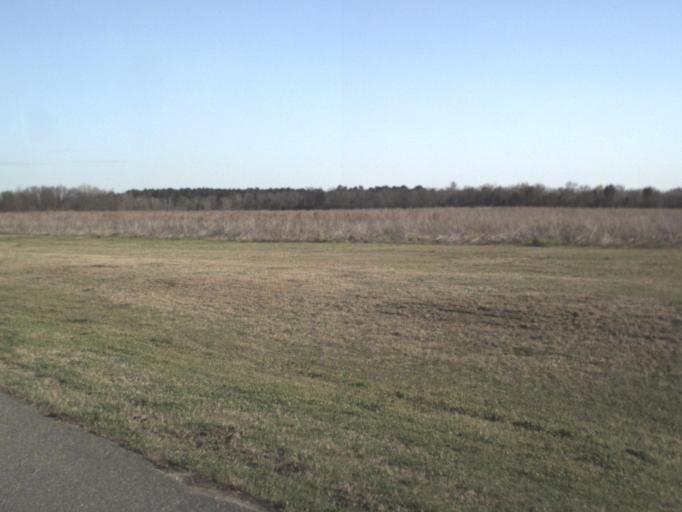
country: US
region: Florida
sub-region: Jackson County
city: Sneads
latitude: 30.7077
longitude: -84.8956
